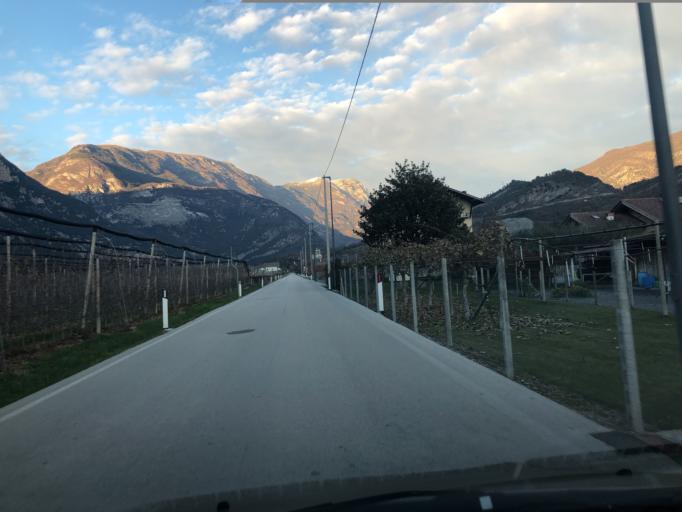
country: IT
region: Trentino-Alto Adige
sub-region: Provincia di Trento
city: Pietramurata
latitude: 46.0285
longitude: 10.9581
